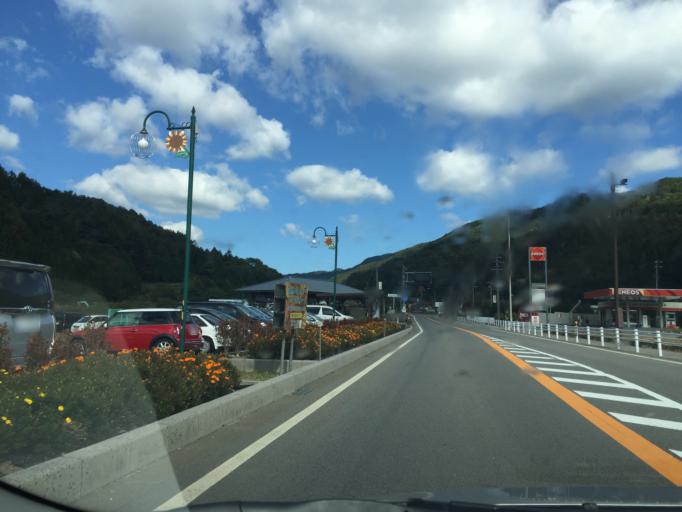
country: JP
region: Gifu
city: Nakatsugawa
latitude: 35.3242
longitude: 137.6324
